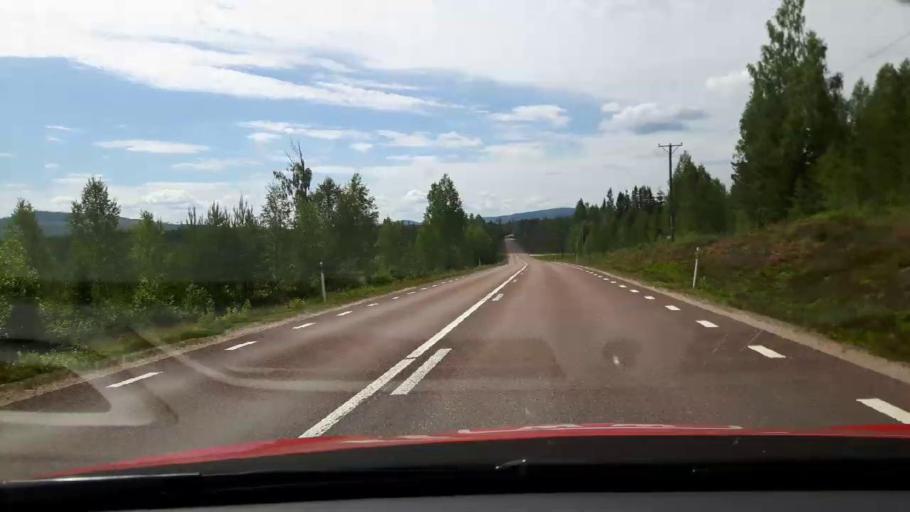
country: SE
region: Jaemtland
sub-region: Harjedalens Kommun
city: Sveg
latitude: 62.0609
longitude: 14.9132
